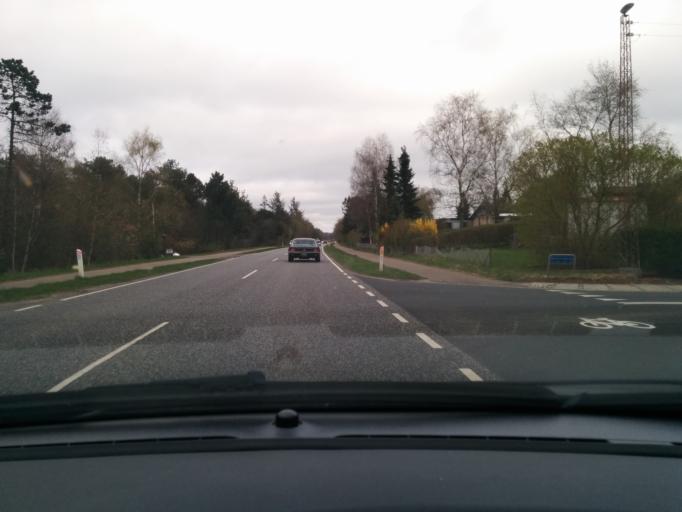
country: DK
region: Central Jutland
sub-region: Silkeborg Kommune
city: Svejbaek
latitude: 56.1744
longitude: 9.6178
